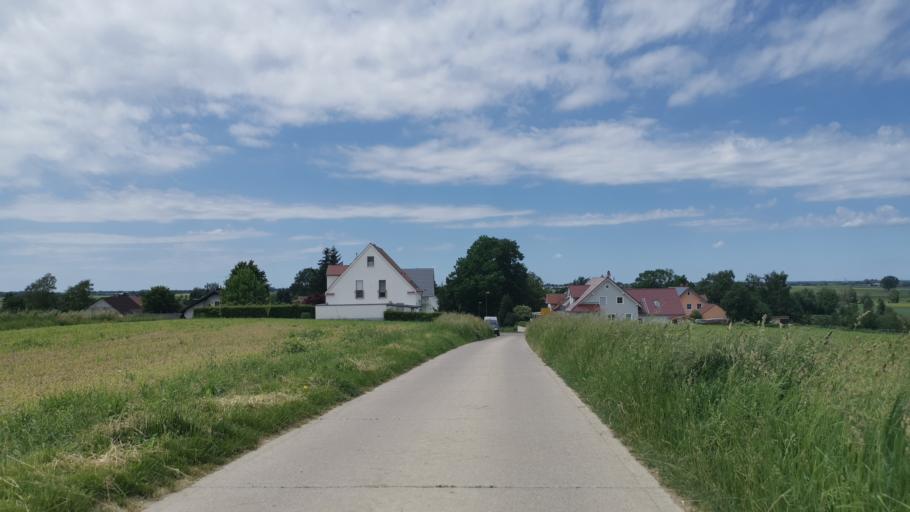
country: DE
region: Bavaria
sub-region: Swabia
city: Steindorf
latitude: 48.2384
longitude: 11.0212
